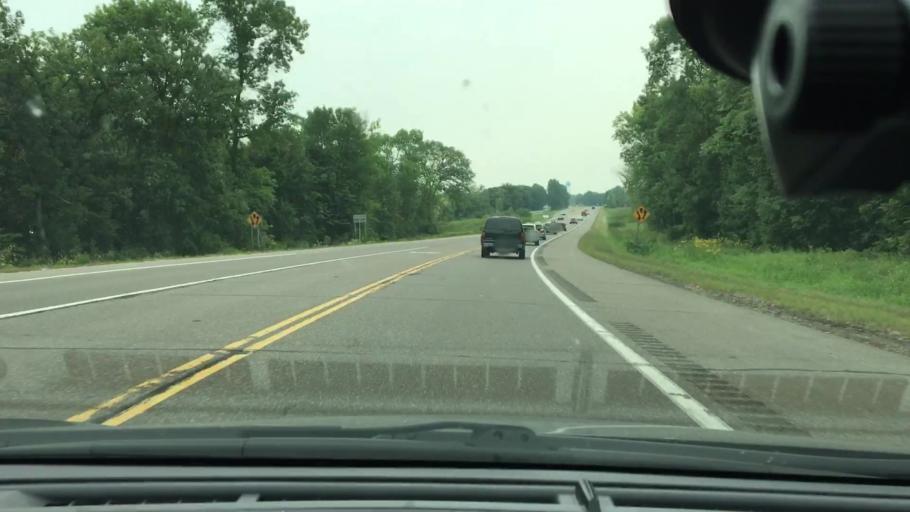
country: US
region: Minnesota
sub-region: Mille Lacs County
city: Vineland
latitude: 46.1994
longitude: -93.7654
